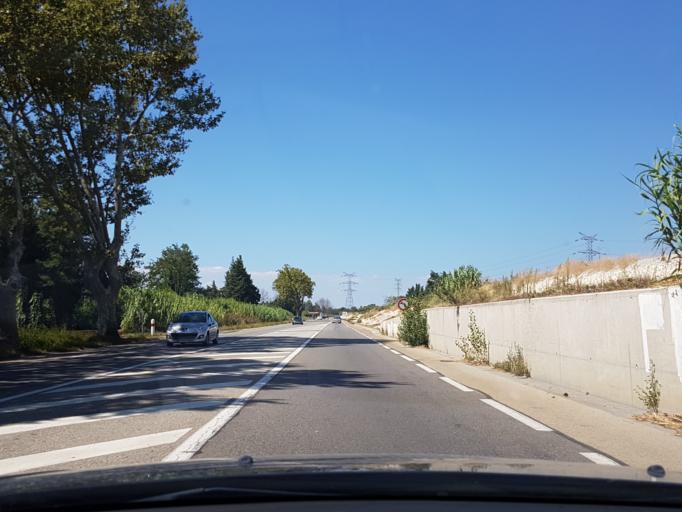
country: FR
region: Provence-Alpes-Cote d'Azur
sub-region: Departement des Bouches-du-Rhone
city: Rognonas
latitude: 43.9080
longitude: 4.8124
